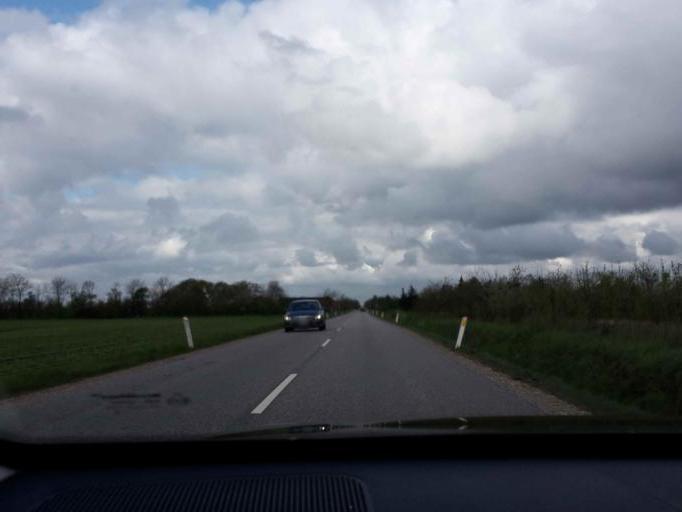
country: DK
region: South Denmark
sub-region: Billund Kommune
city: Grindsted
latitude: 55.7765
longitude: 8.8450
